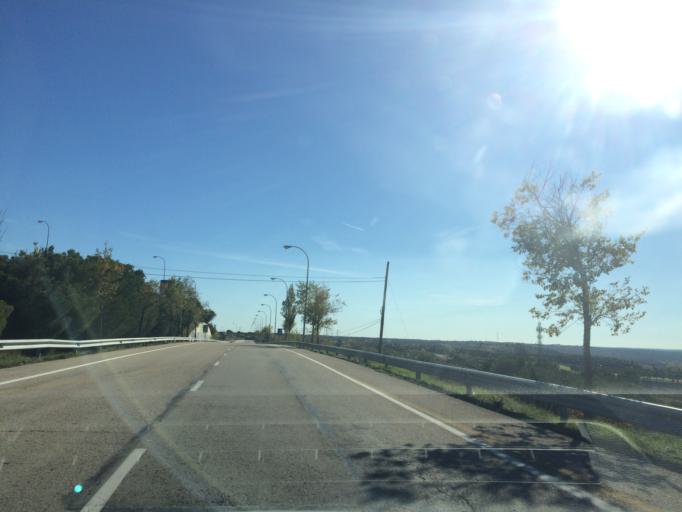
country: ES
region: Madrid
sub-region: Provincia de Madrid
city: Tres Cantos
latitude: 40.6105
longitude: -3.7228
